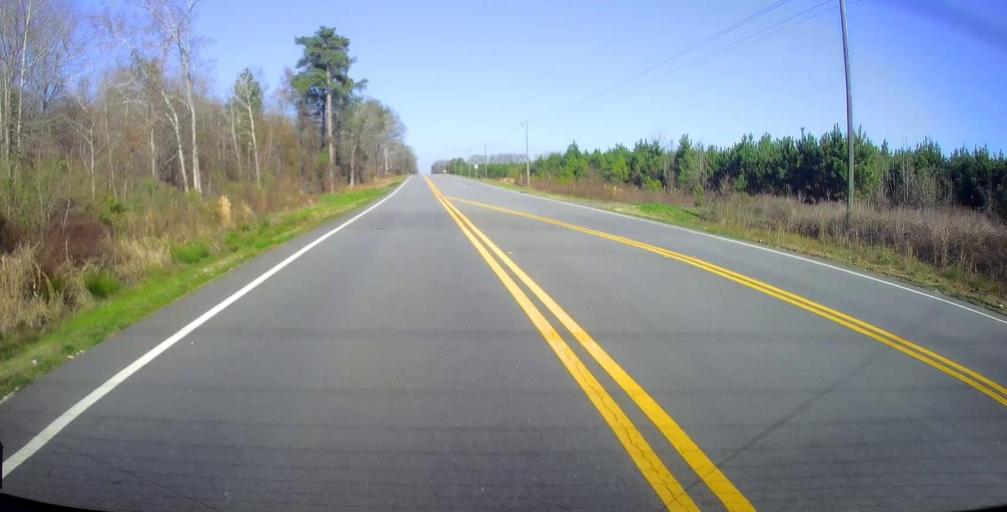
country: US
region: Georgia
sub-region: Macon County
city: Marshallville
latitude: 32.3270
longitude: -83.8751
